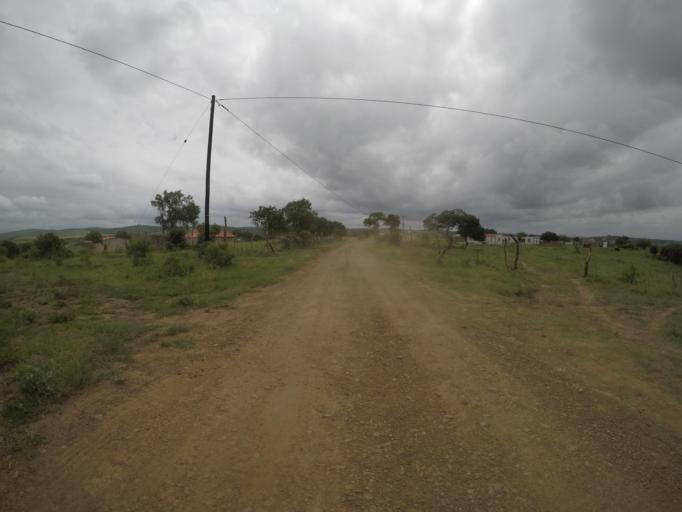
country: ZA
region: KwaZulu-Natal
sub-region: uThungulu District Municipality
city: Empangeni
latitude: -28.6002
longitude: 31.8331
